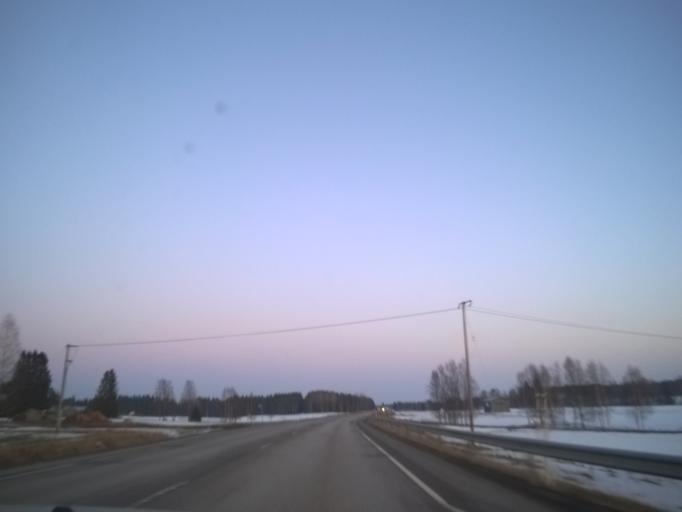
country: FI
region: Northern Ostrobothnia
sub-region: Nivala-Haapajaervi
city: Pyhaejaervi
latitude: 63.8241
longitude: 25.8861
